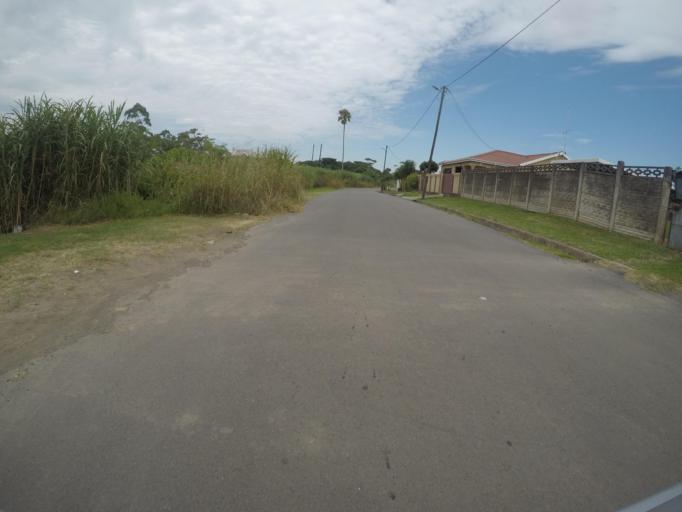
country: ZA
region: Eastern Cape
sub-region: Buffalo City Metropolitan Municipality
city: East London
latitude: -32.9917
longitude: 27.8804
